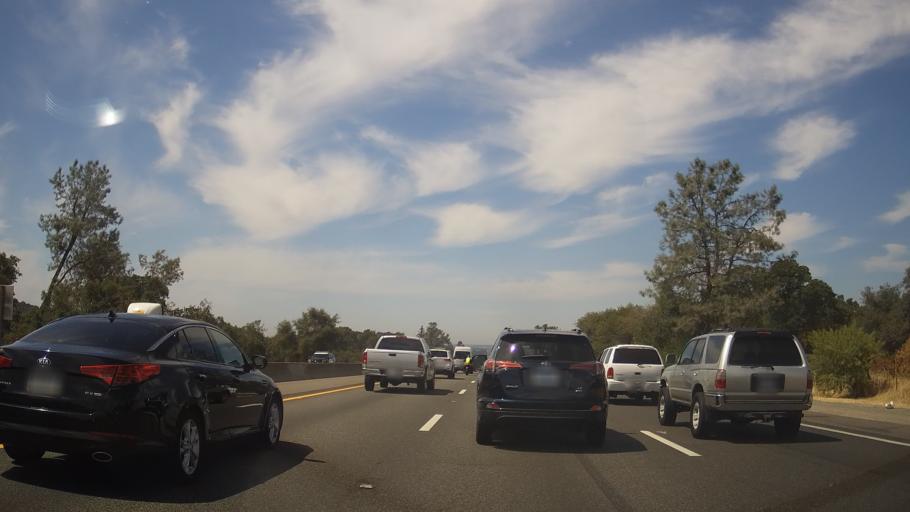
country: US
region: California
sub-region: Placer County
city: Newcastle
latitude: 38.8608
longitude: -121.1368
